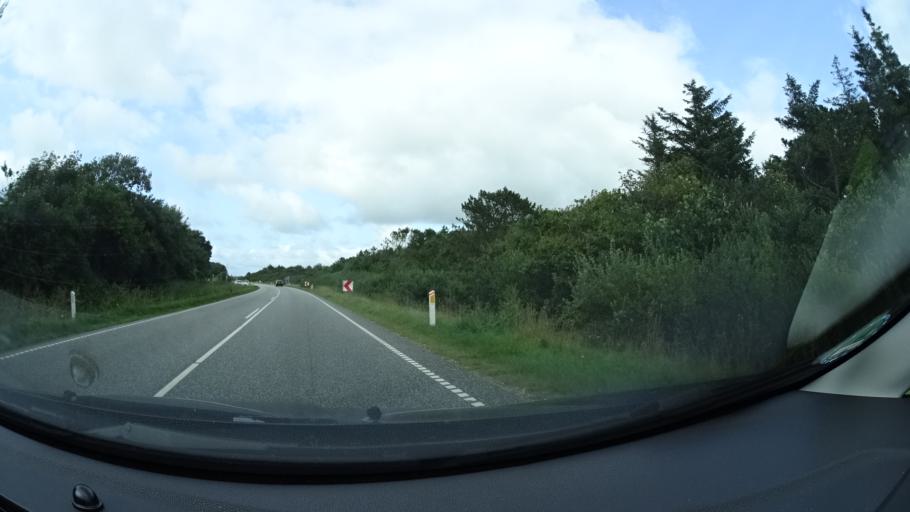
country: DK
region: Central Jutland
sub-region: Lemvig Kommune
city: Harboore
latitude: 56.6187
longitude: 8.1878
